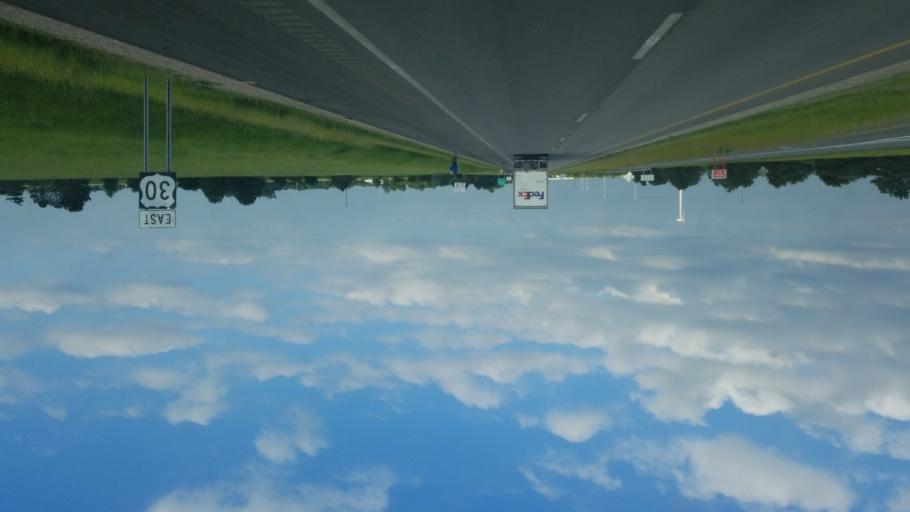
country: US
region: Ohio
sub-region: Van Wert County
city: Convoy
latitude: 40.9400
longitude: -84.7074
